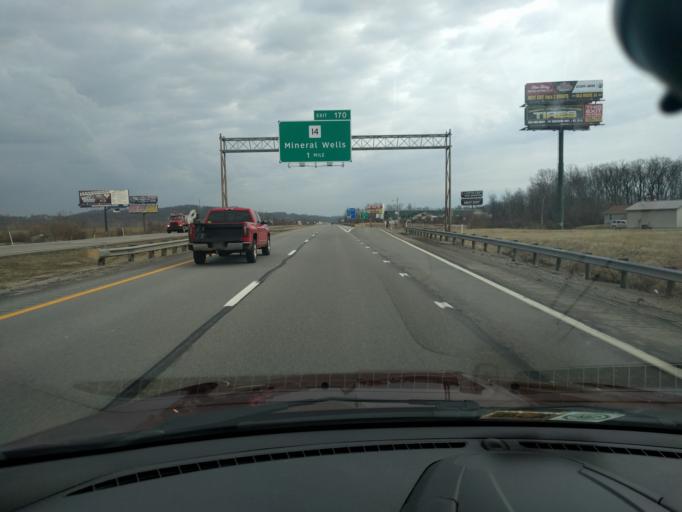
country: US
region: West Virginia
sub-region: Wood County
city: Mineral Wells
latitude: 39.1691
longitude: -81.5389
